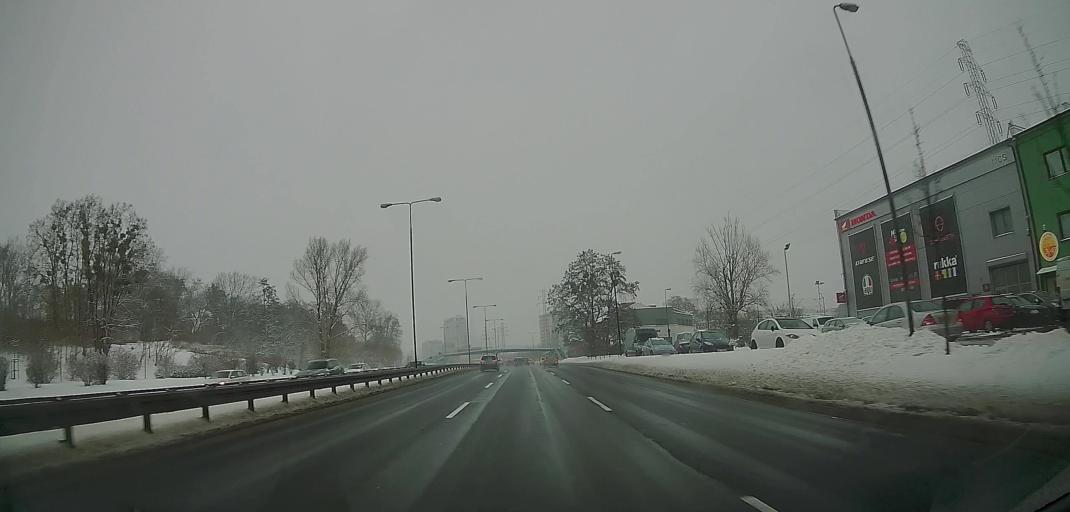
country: PL
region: Masovian Voivodeship
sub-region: Warszawa
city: Wola
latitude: 52.2414
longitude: 20.9575
